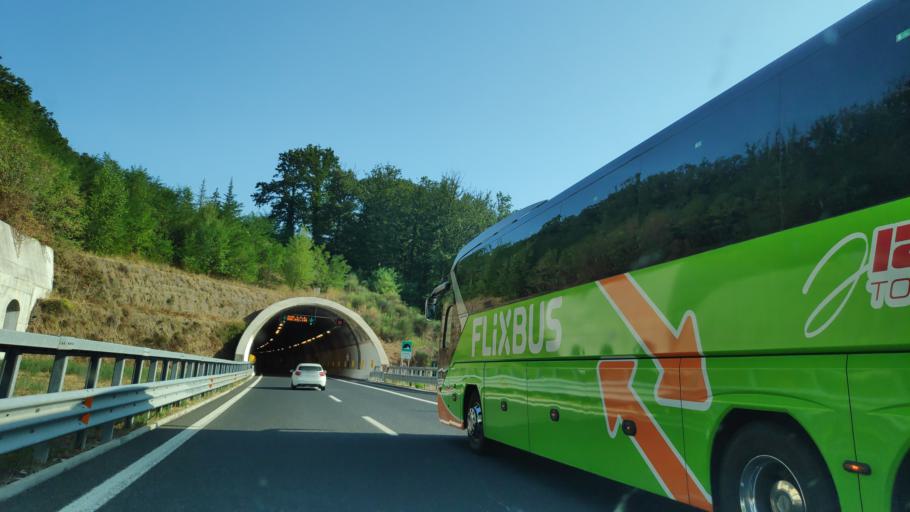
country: IT
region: Campania
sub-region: Provincia di Salerno
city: Buonabitacolo
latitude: 40.2523
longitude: 15.6604
